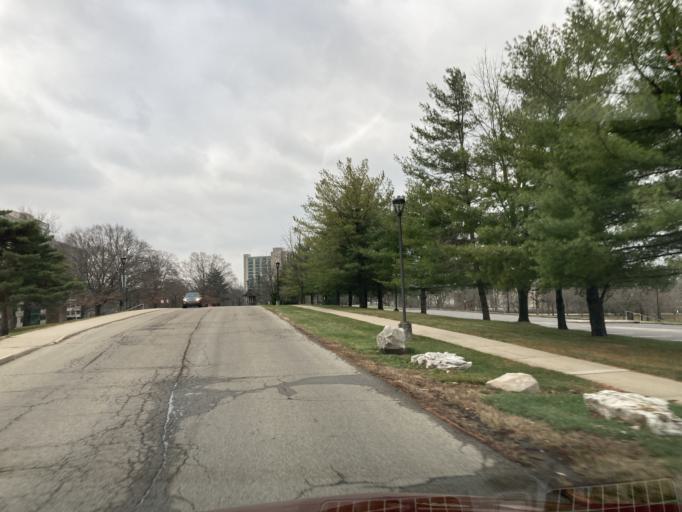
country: US
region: Indiana
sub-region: Monroe County
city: Bloomington
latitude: 39.1747
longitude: -86.5105
